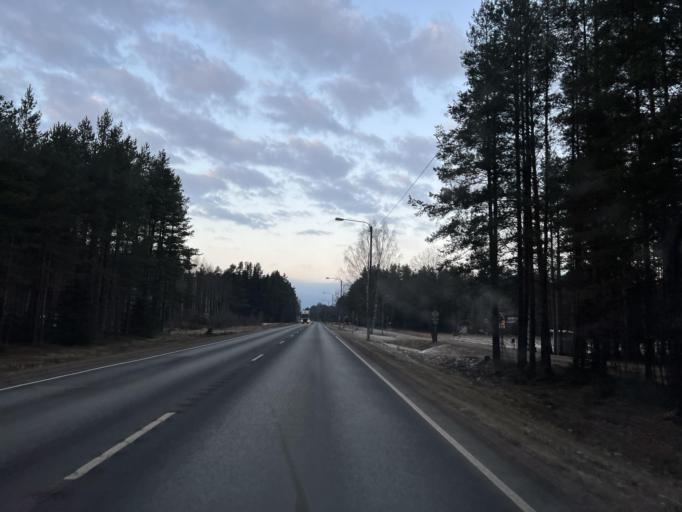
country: FI
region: Northern Ostrobothnia
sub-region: Oulu
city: Muhos
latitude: 64.8764
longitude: 25.8558
